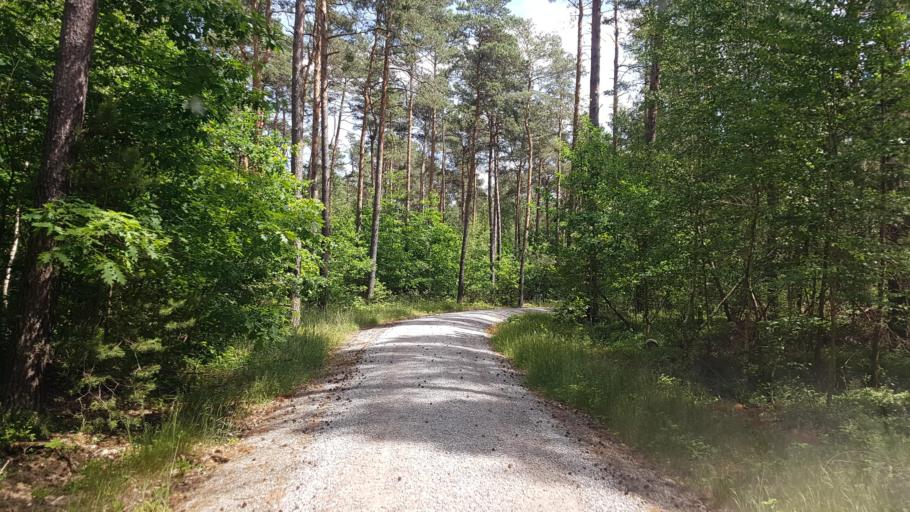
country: DE
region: Brandenburg
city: Plessa
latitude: 51.4953
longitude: 13.6023
